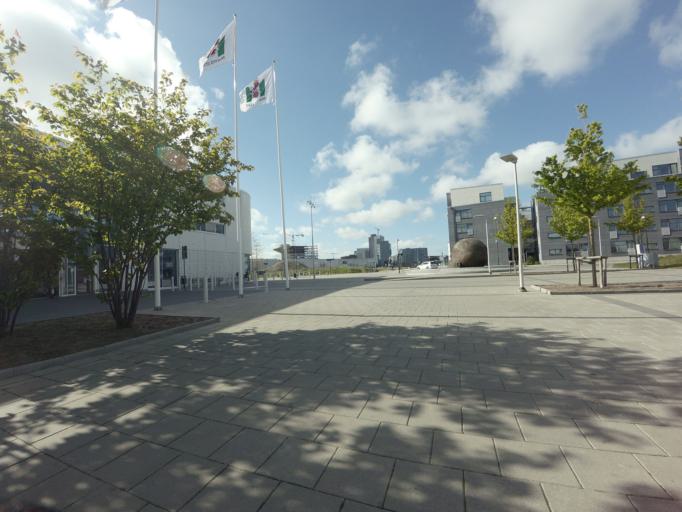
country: SE
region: Skane
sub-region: Malmo
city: Malmoe
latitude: 55.5705
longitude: 12.9768
